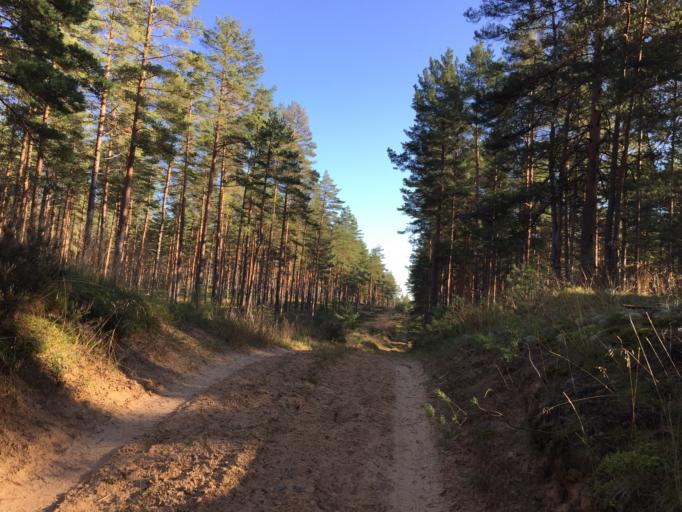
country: LV
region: Garkalne
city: Garkalne
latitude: 57.0209
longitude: 24.3656
